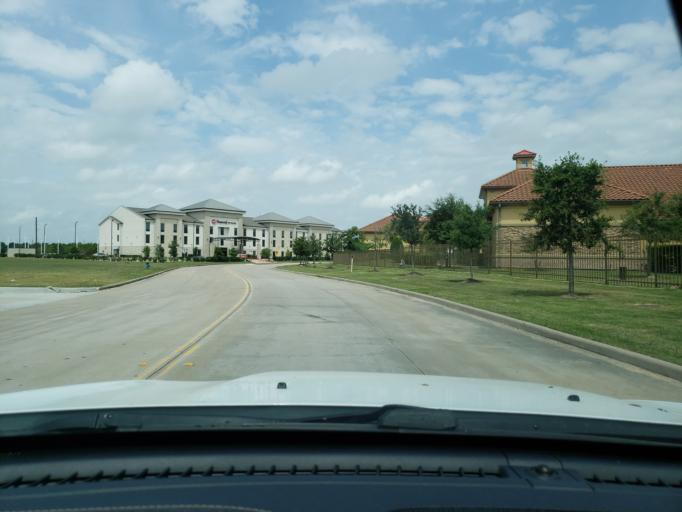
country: US
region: Texas
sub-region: Fort Bend County
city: Cinco Ranch
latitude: 29.7878
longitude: -95.7298
